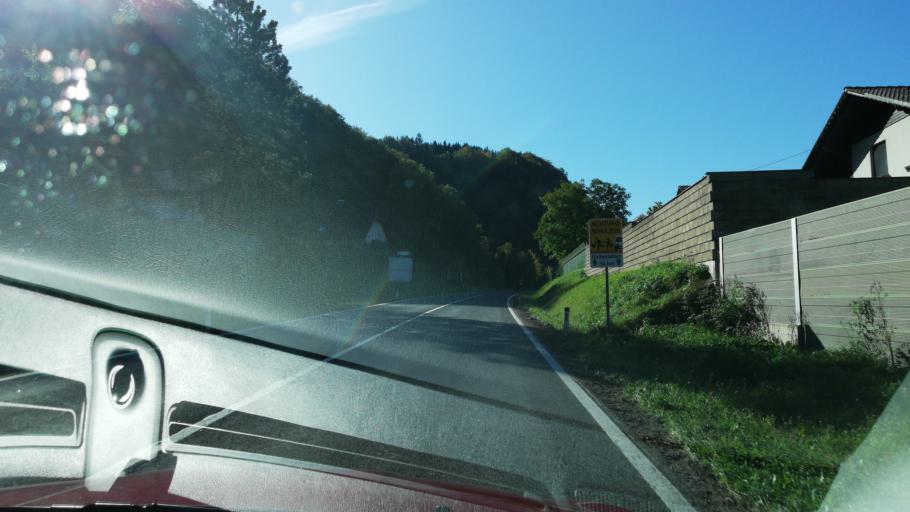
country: AT
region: Upper Austria
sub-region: Politischer Bezirk Steyr-Land
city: Weyer
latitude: 47.8245
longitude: 14.6456
